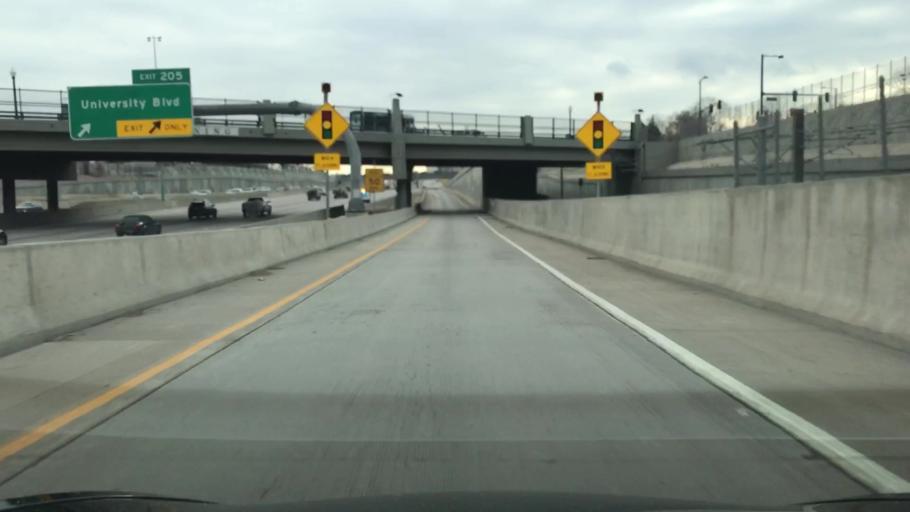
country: US
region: Colorado
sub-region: Arapahoe County
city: Glendale
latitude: 39.6900
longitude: -104.9743
